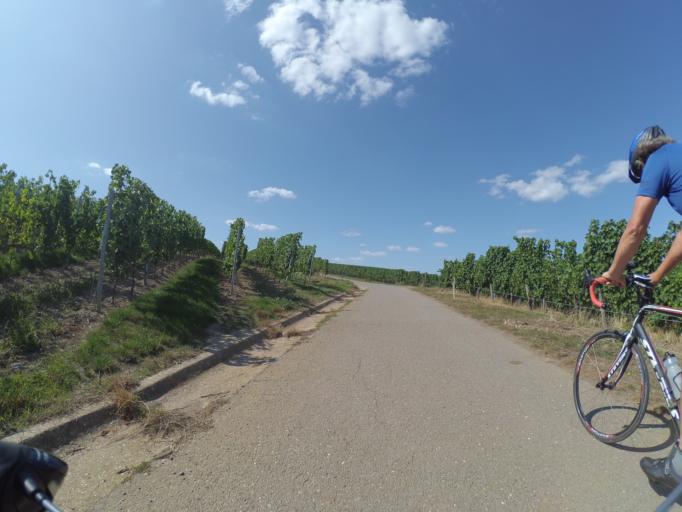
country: DE
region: Rheinland-Pfalz
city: Longuich
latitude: 49.7993
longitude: 6.7628
